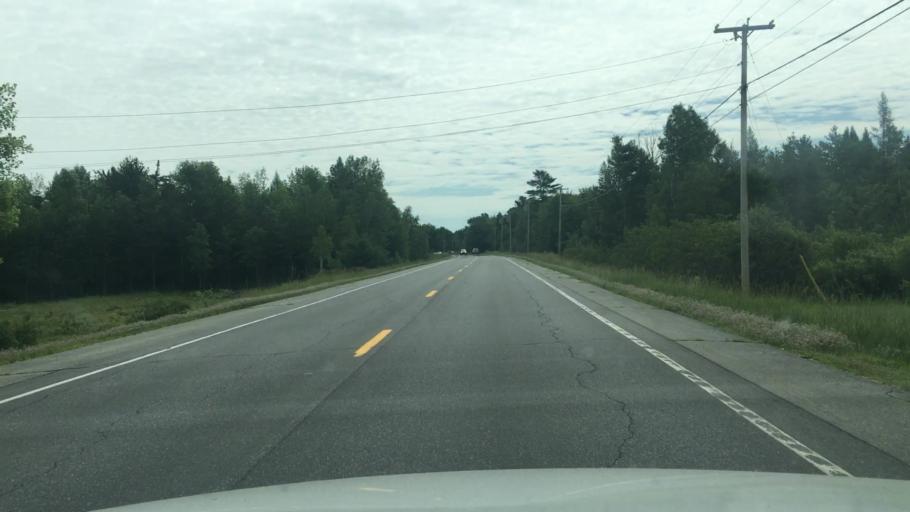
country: US
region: Maine
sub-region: Waldo County
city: Burnham
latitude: 44.6149
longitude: -69.3756
